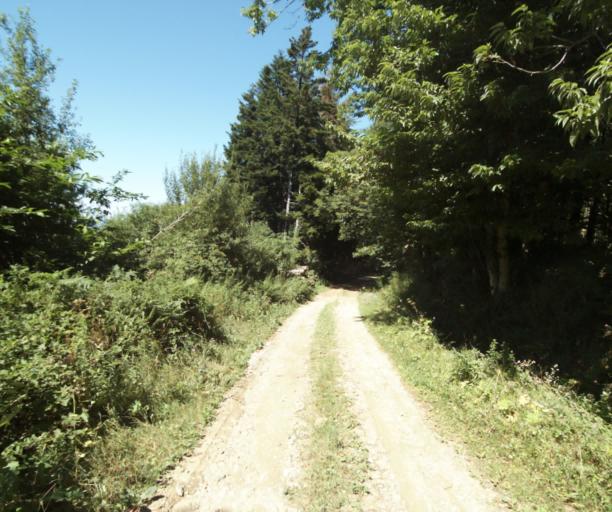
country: FR
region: Midi-Pyrenees
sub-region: Departement du Tarn
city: Soreze
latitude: 43.4428
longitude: 2.1075
